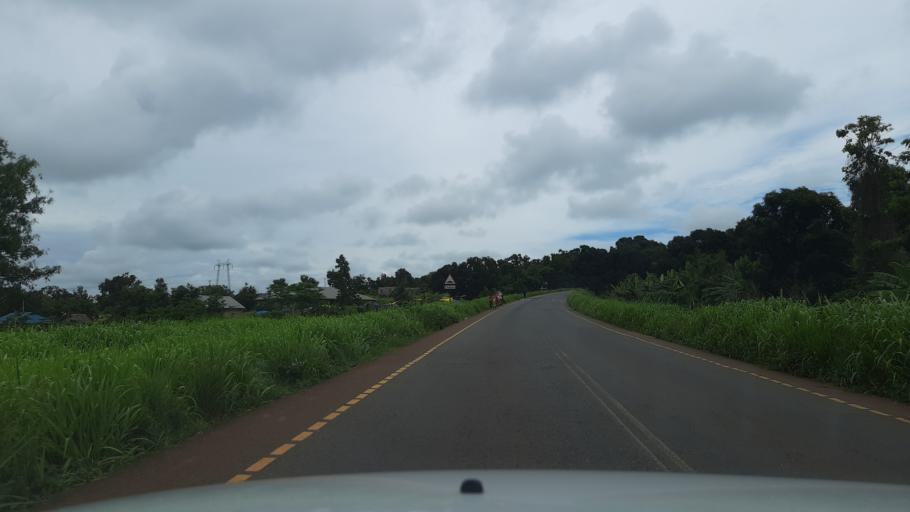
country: TZ
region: Pwani
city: Lugoba
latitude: -6.0863
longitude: 38.2448
